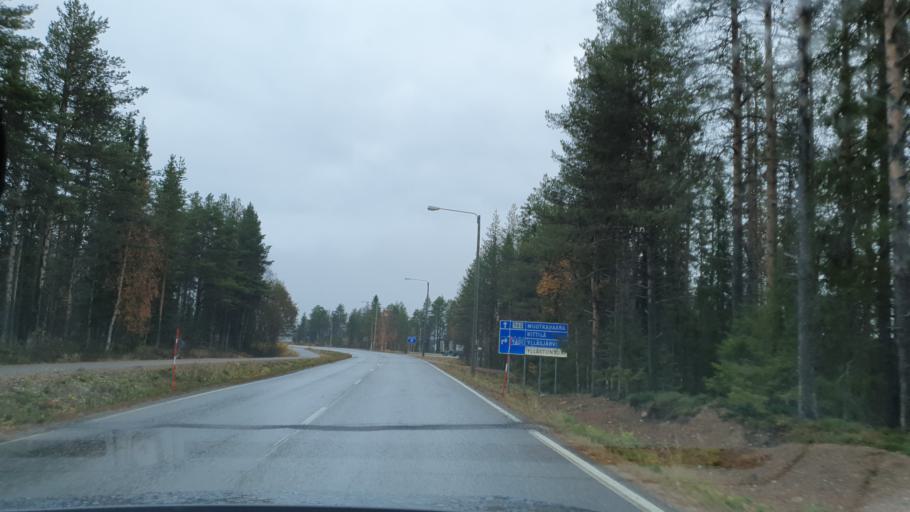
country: FI
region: Lapland
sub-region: Tunturi-Lappi
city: Kolari
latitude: 67.6040
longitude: 24.1382
